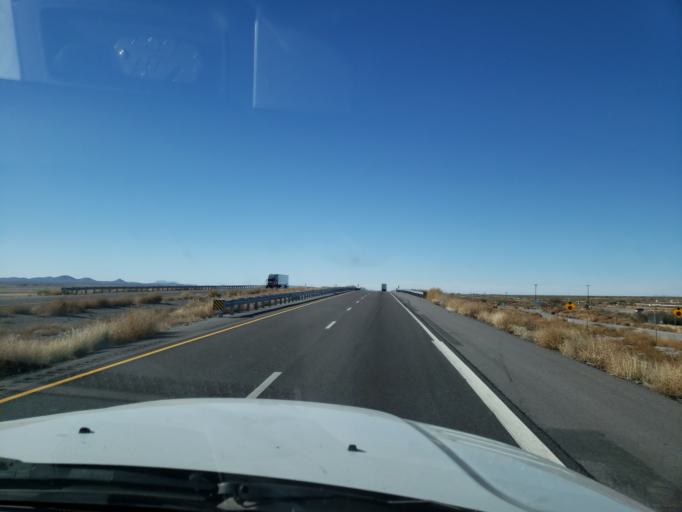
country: US
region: New Mexico
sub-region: Hidalgo County
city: Lordsburg
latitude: 32.3111
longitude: -108.6054
